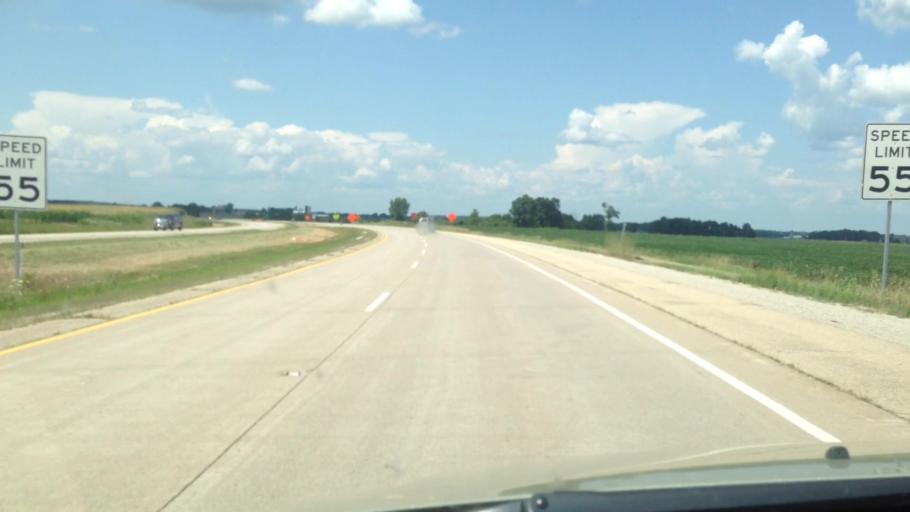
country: US
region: Wisconsin
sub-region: Brown County
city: Pulaski
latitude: 44.6819
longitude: -88.3120
